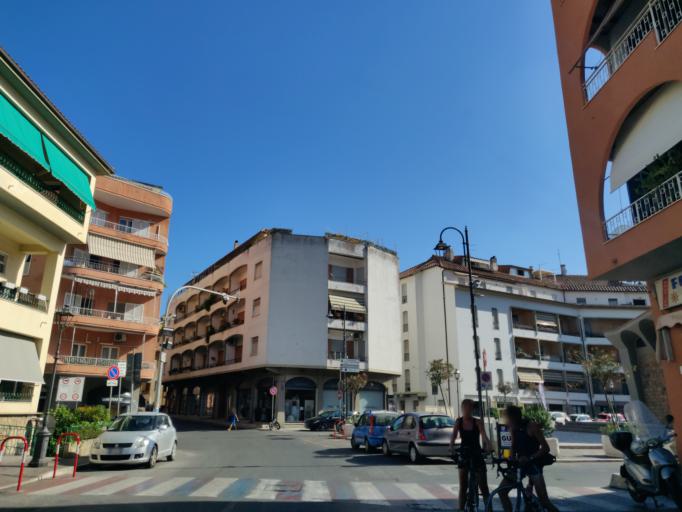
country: IT
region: Tuscany
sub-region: Provincia di Grosseto
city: Porto Ercole
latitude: 42.3938
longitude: 11.2039
